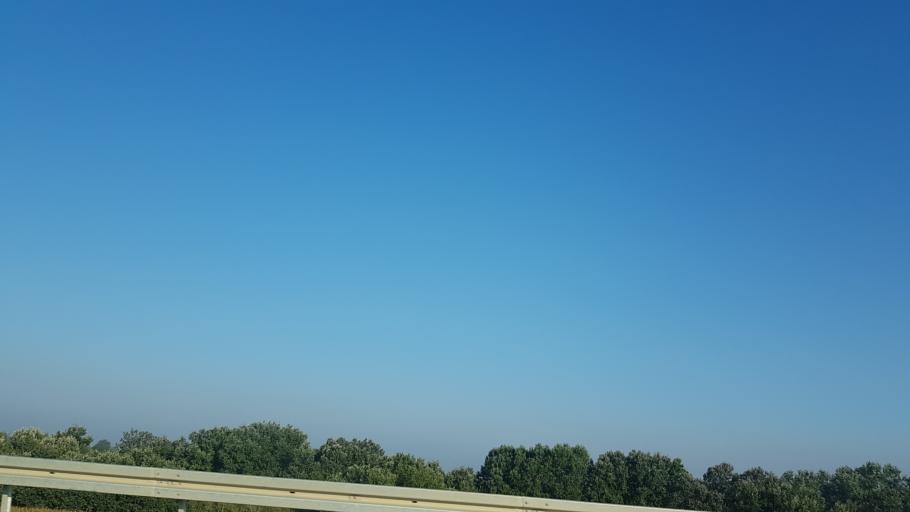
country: TR
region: Bursa
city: Karacabey
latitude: 40.1803
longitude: 28.3293
